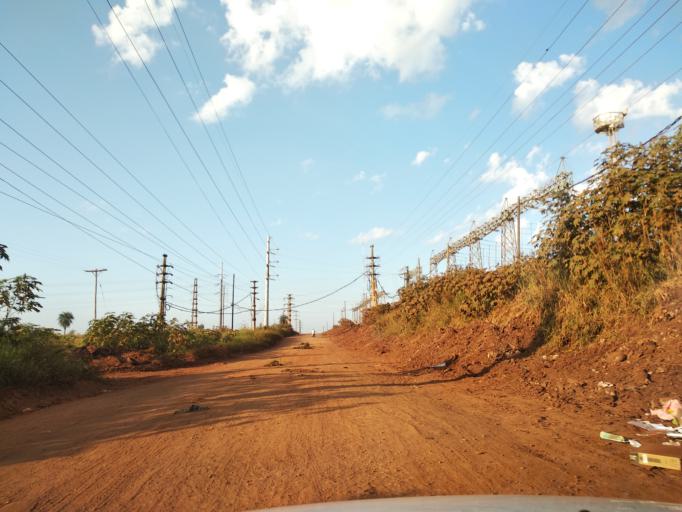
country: AR
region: Misiones
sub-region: Departamento de Capital
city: Posadas
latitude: -27.4412
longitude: -55.9161
